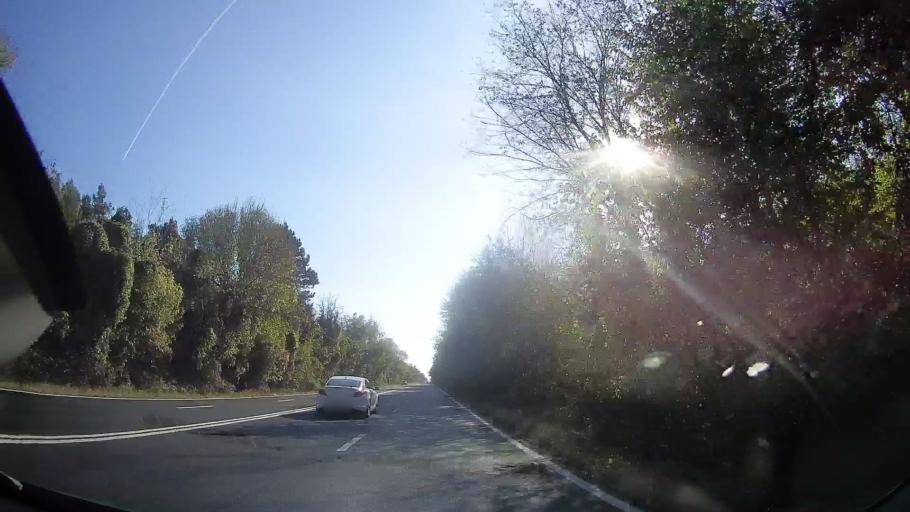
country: RO
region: Constanta
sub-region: Comuna Douazeci si Trei August
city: Dulcesti
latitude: 43.8732
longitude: 28.5742
